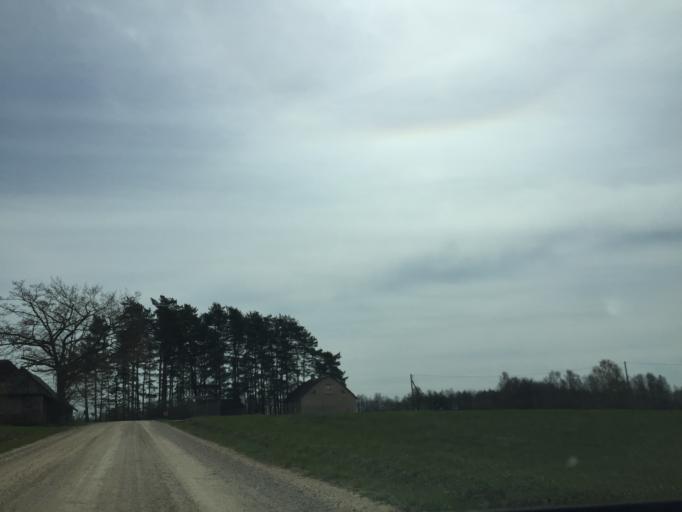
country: LV
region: Ludzas Rajons
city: Ludza
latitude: 56.5652
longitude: 27.5592
